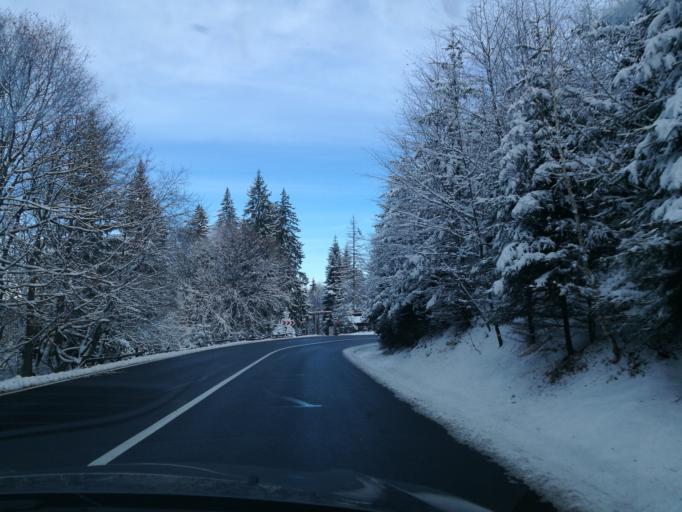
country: RO
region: Brasov
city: Brasov
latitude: 45.6021
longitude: 25.5530
